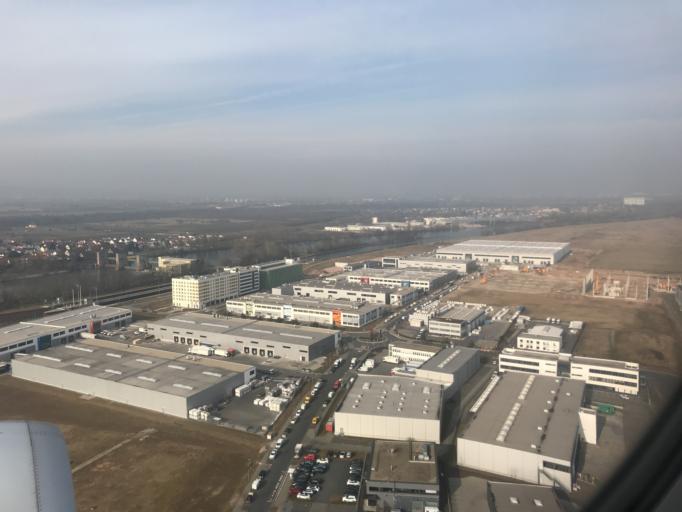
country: DE
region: Hesse
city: Raunheim
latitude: 50.0321
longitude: 8.4763
